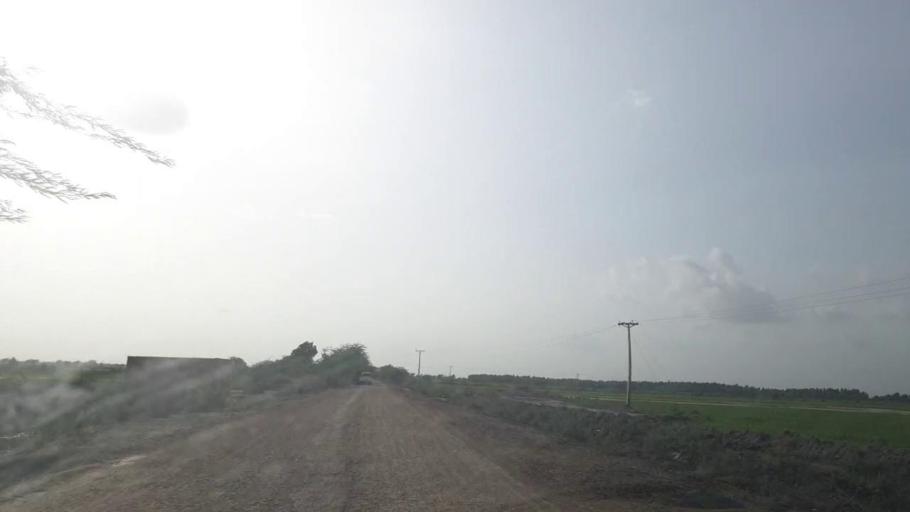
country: PK
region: Sindh
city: Tando Bago
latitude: 24.7647
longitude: 69.0763
